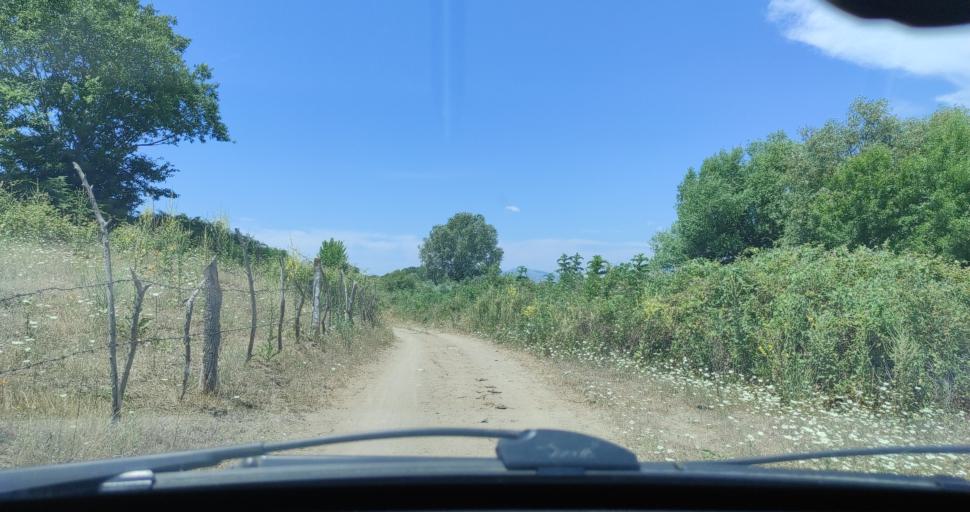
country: AL
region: Shkoder
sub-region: Rrethi i Shkodres
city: Velipoje
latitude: 41.8834
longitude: 19.3903
